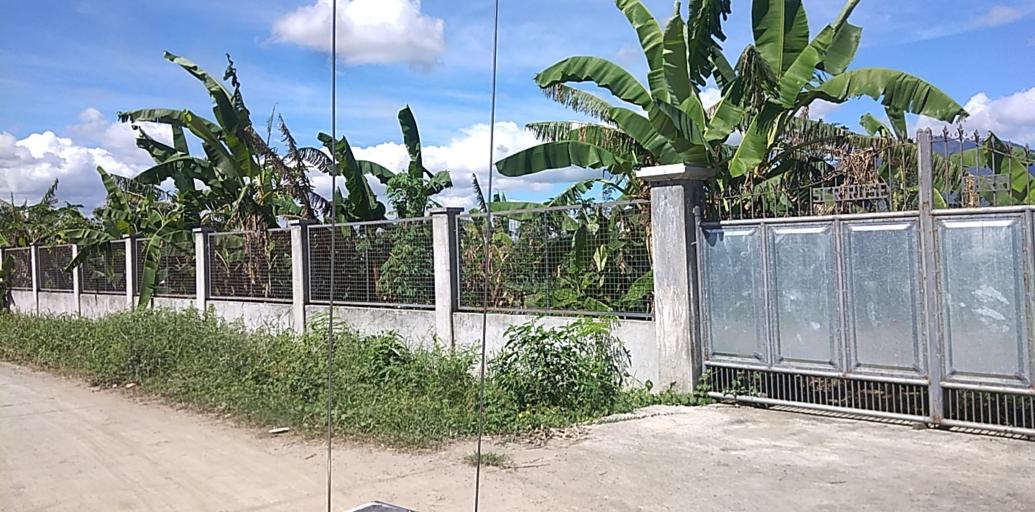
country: PH
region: Central Luzon
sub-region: Province of Pampanga
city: Arayat
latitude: 15.1278
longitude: 120.7858
